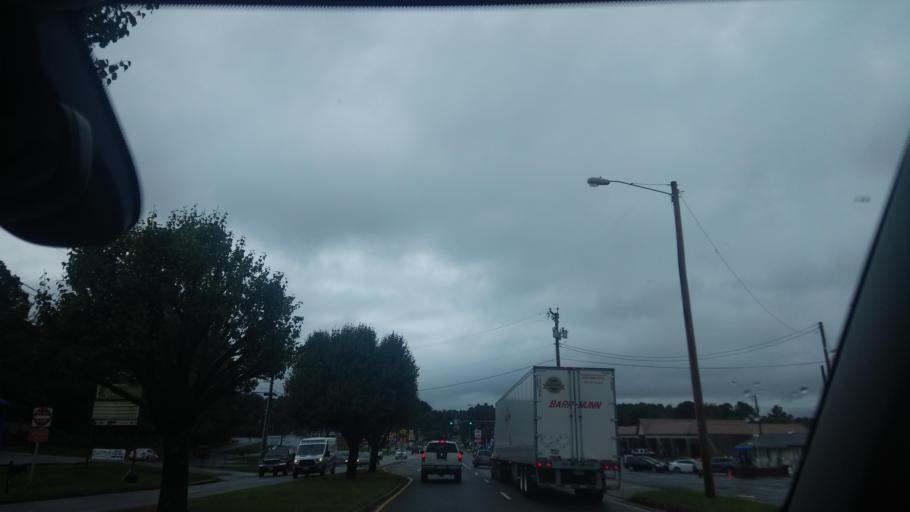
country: US
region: Virginia
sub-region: City of Galax
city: Galax
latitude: 36.6824
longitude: -80.8929
